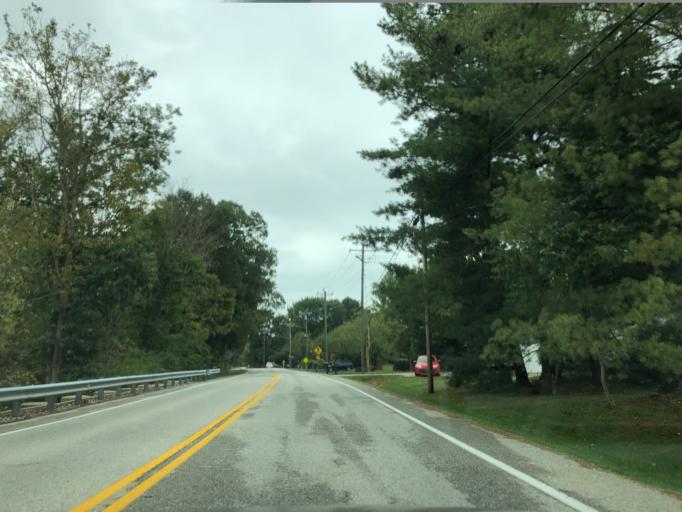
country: US
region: Ohio
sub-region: Hamilton County
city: The Village of Indian Hill
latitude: 39.2616
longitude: -84.3086
